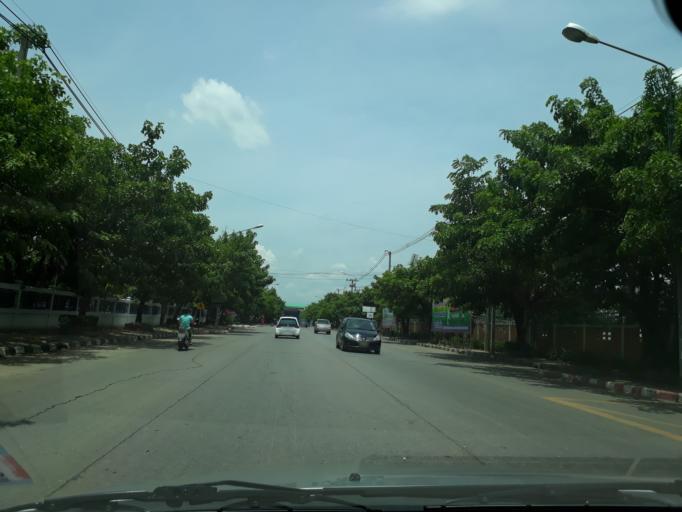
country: TH
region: Khon Kaen
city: Khon Kaen
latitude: 16.4146
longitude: 102.8261
